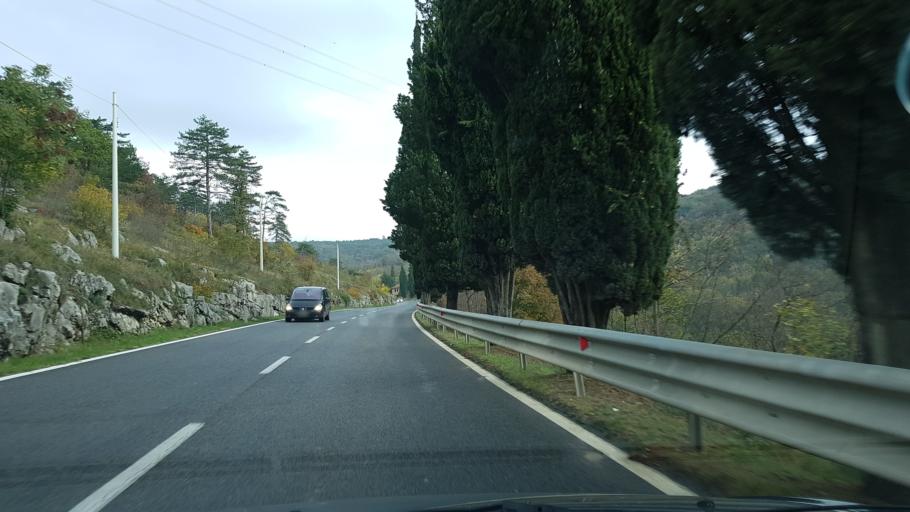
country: IT
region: Friuli Venezia Giulia
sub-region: Provincia di Gorizia
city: Savogna d'Isonzo
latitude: 45.8702
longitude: 13.5754
